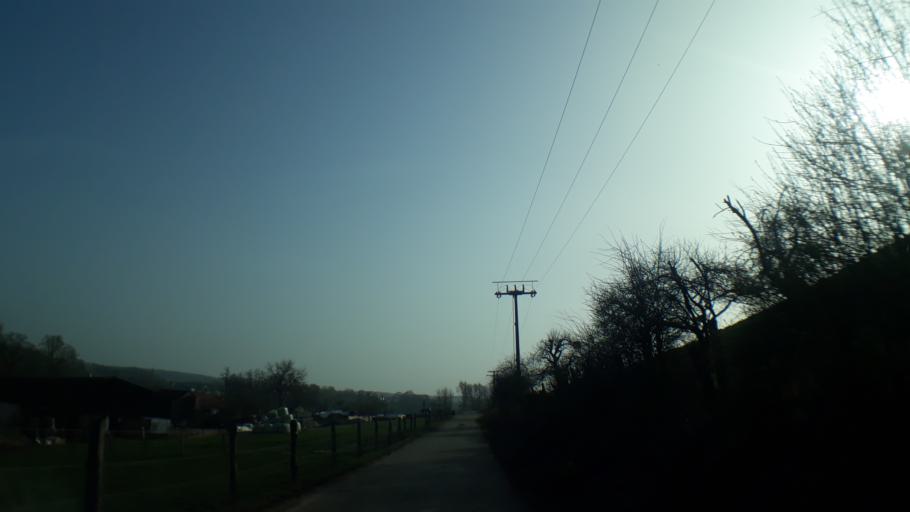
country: DE
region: North Rhine-Westphalia
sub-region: Regierungsbezirk Koln
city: Bad Munstereifel
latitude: 50.5567
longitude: 6.7206
